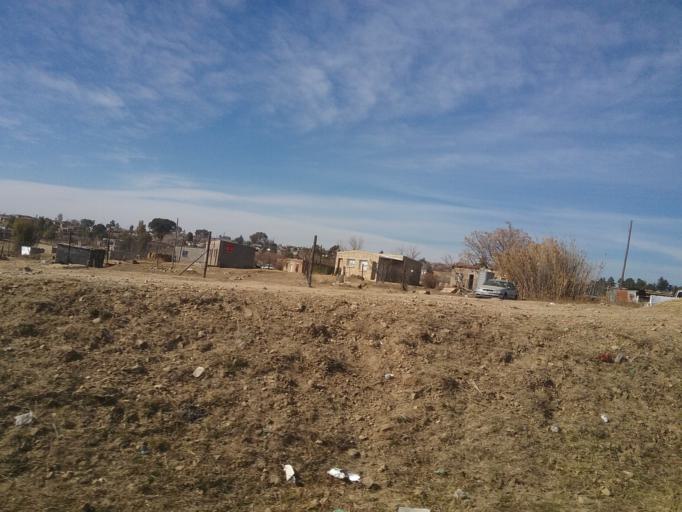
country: LS
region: Maseru
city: Maseru
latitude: -29.4120
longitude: 27.5587
